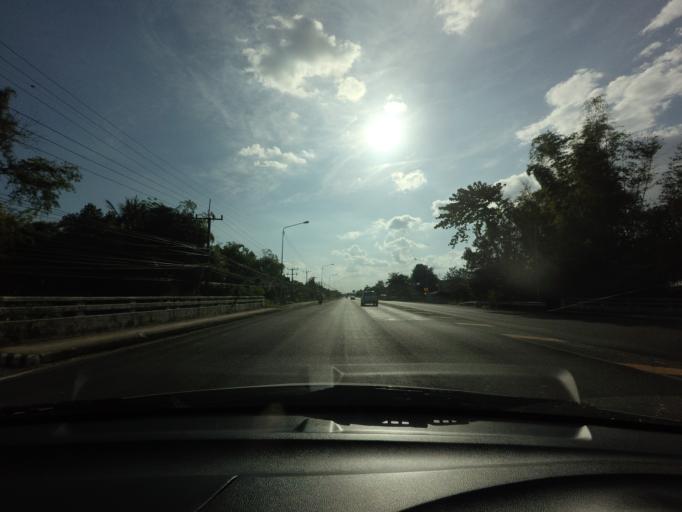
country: TH
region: Nakhon Nayok
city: Nakhon Nayok
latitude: 14.2523
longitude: 101.2582
